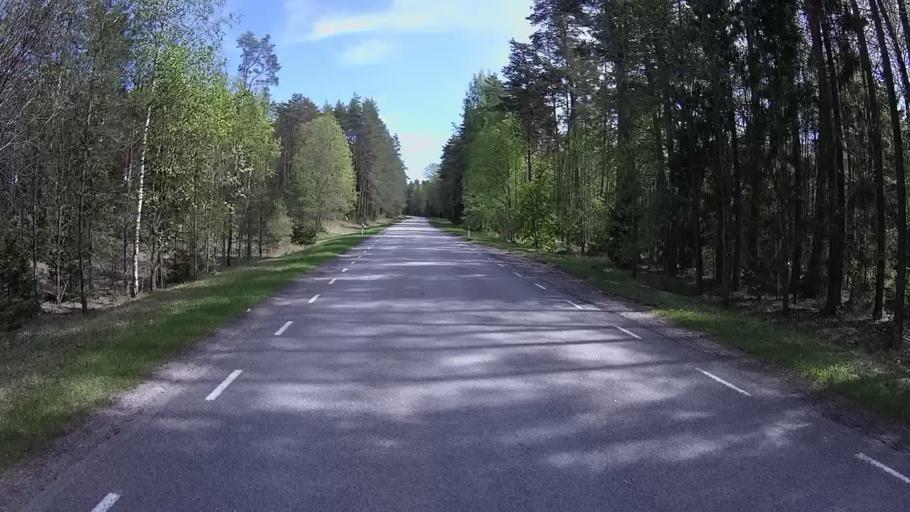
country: LV
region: Apes Novads
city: Ape
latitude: 57.6073
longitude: 26.4587
